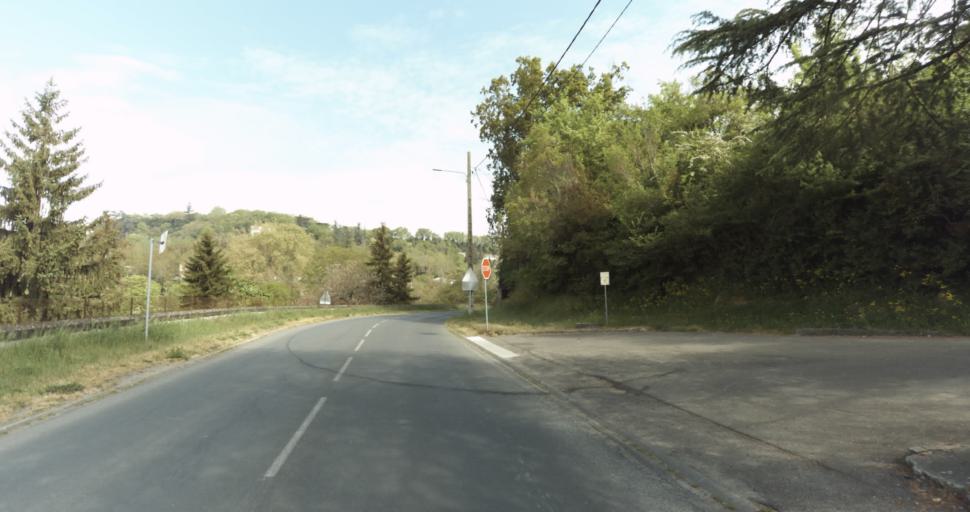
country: FR
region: Aquitaine
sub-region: Departement du Lot-et-Garonne
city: Le Passage
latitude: 44.2145
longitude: 0.6068
